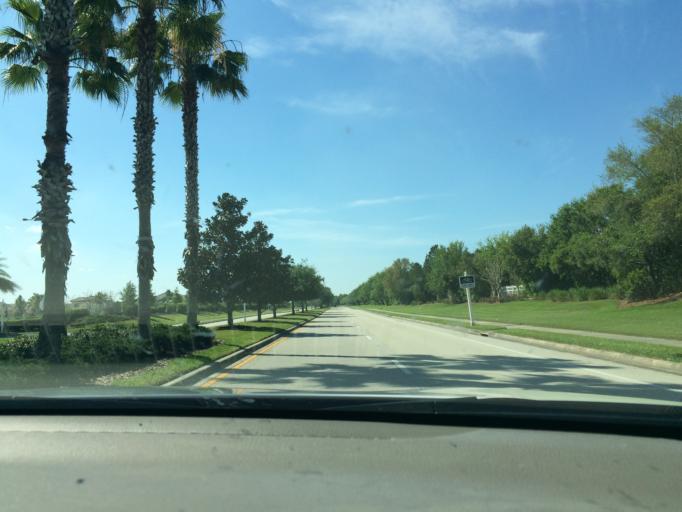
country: US
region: Florida
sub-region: Sarasota County
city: The Meadows
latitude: 27.4069
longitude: -82.3996
